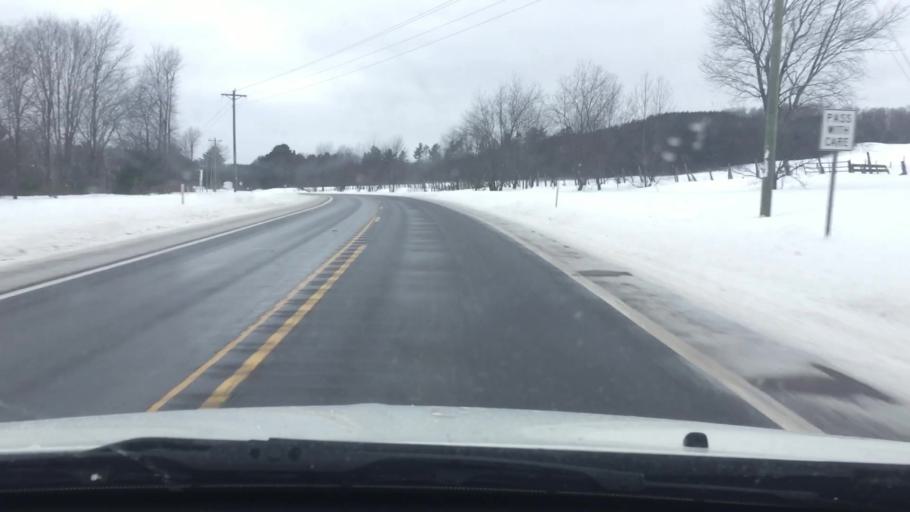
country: US
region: Michigan
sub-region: Charlevoix County
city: Boyne City
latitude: 45.0942
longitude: -84.9529
